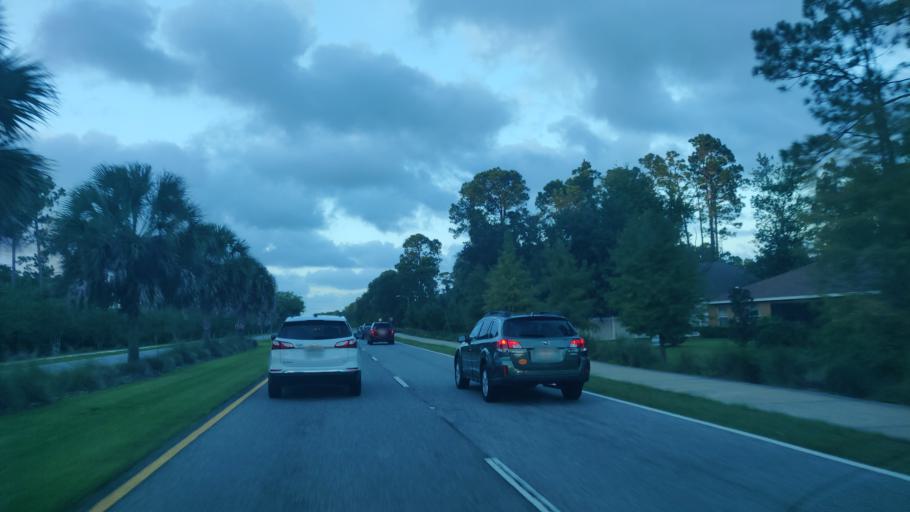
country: US
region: Florida
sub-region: Flagler County
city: Bunnell
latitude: 29.5009
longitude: -81.2195
